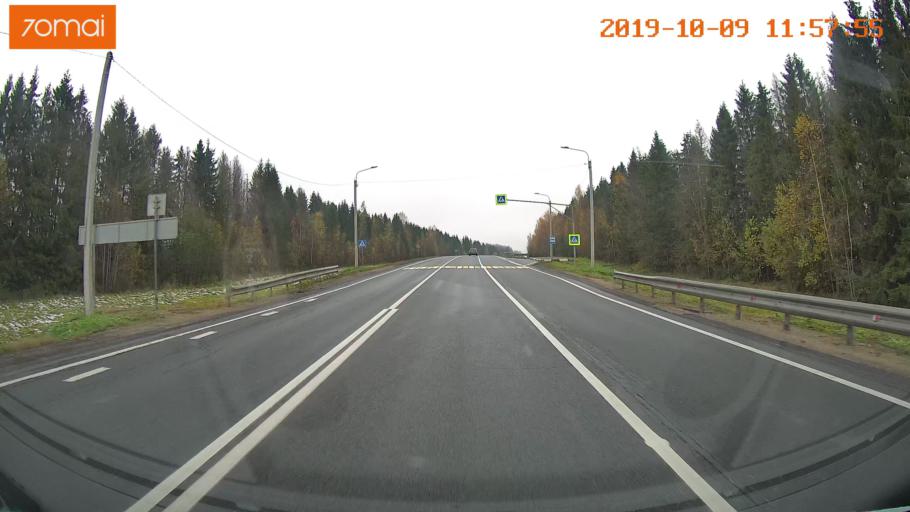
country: RU
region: Vologda
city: Gryazovets
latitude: 58.7255
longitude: 40.2953
